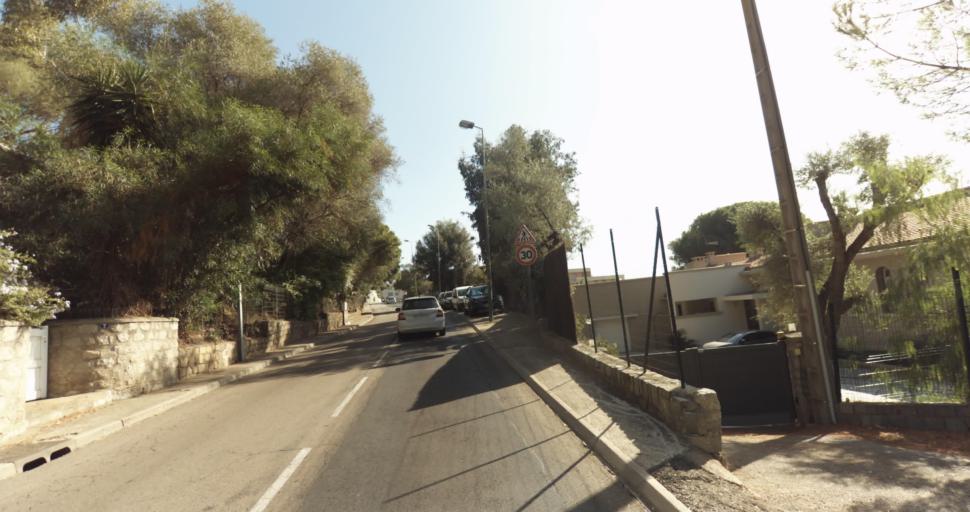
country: FR
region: Corsica
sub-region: Departement de la Corse-du-Sud
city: Ajaccio
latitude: 41.9178
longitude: 8.7249
